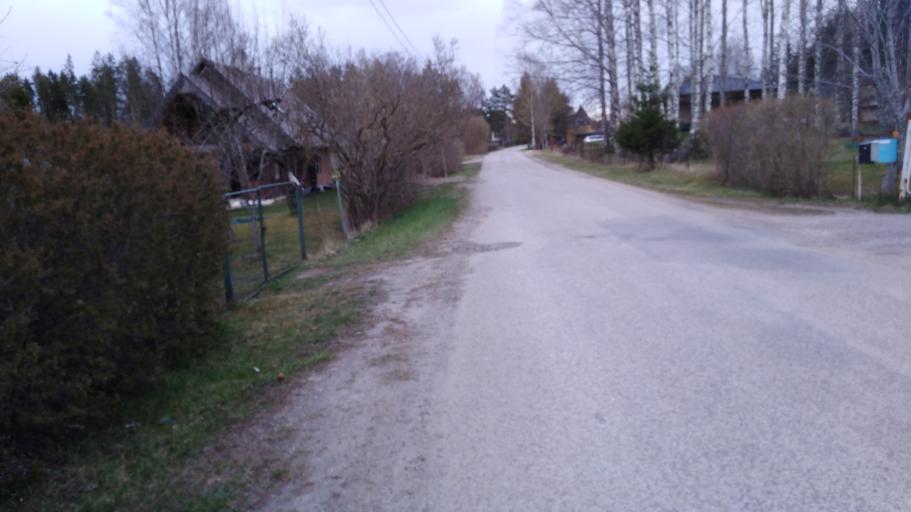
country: EE
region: Vorumaa
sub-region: Voru linn
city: Voru
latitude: 57.8076
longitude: 27.0177
